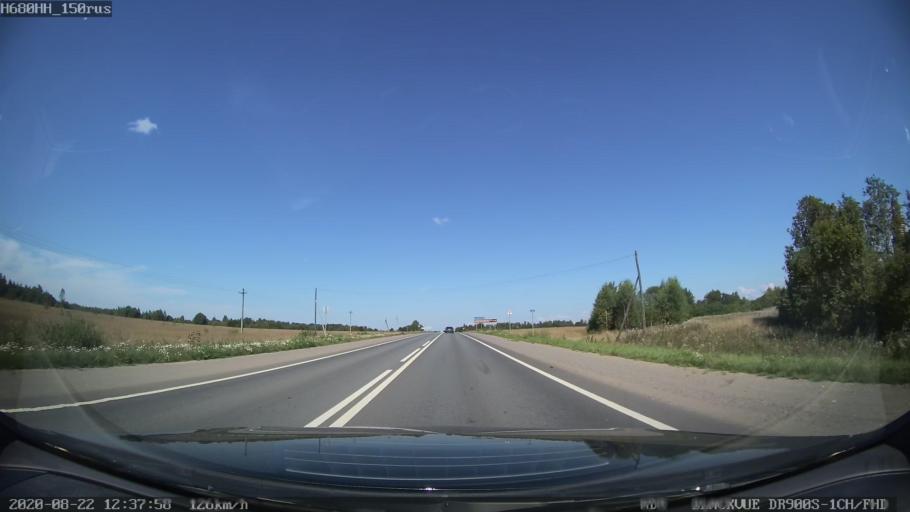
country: RU
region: Tverskaya
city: Rameshki
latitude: 57.3060
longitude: 36.0888
